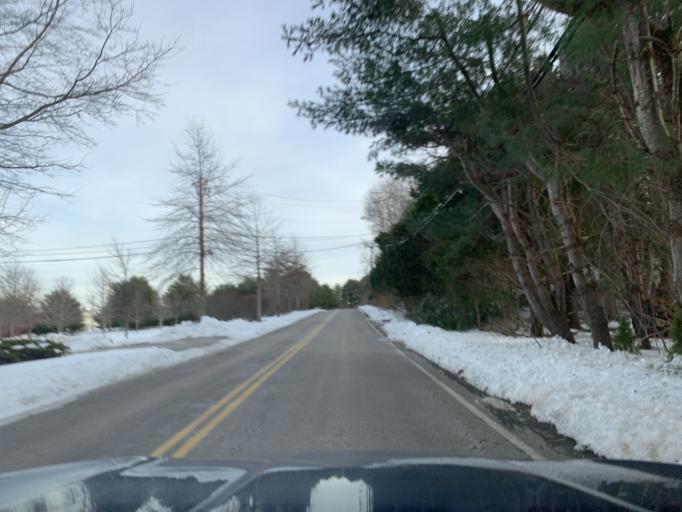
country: US
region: Rhode Island
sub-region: Washington County
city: North Kingstown
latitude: 41.5905
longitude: -71.4363
